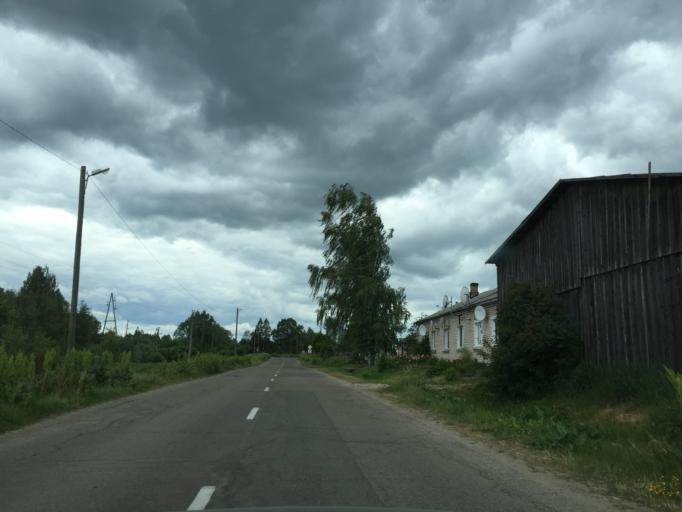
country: LV
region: Rezekne
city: Rezekne
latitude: 56.3566
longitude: 27.1514
